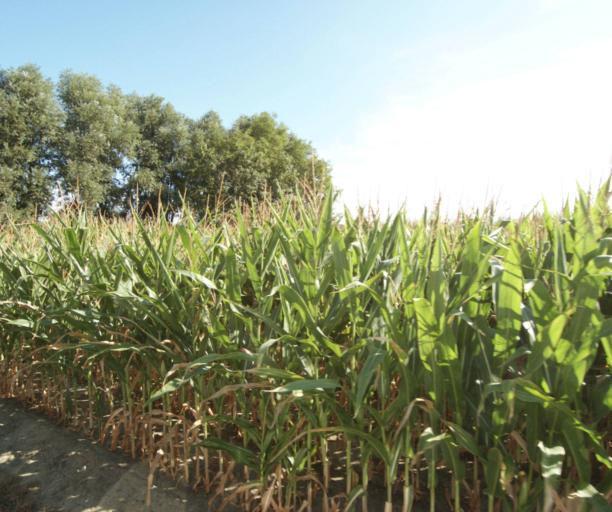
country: FR
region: Nord-Pas-de-Calais
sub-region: Departement du Nord
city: Roncq
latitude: 50.7680
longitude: 3.1291
